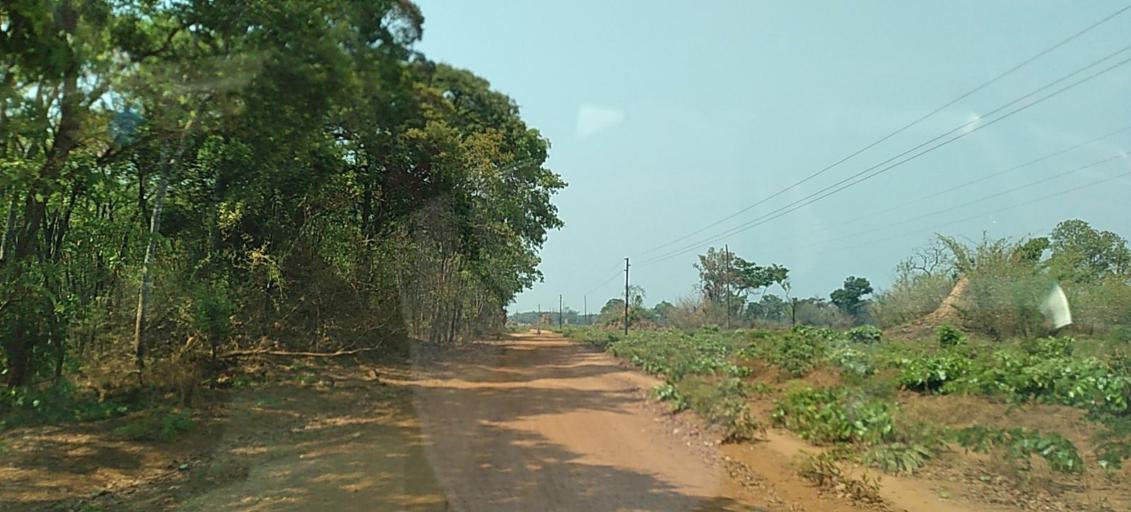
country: ZM
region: Copperbelt
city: Kalulushi
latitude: -13.0862
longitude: 27.4092
